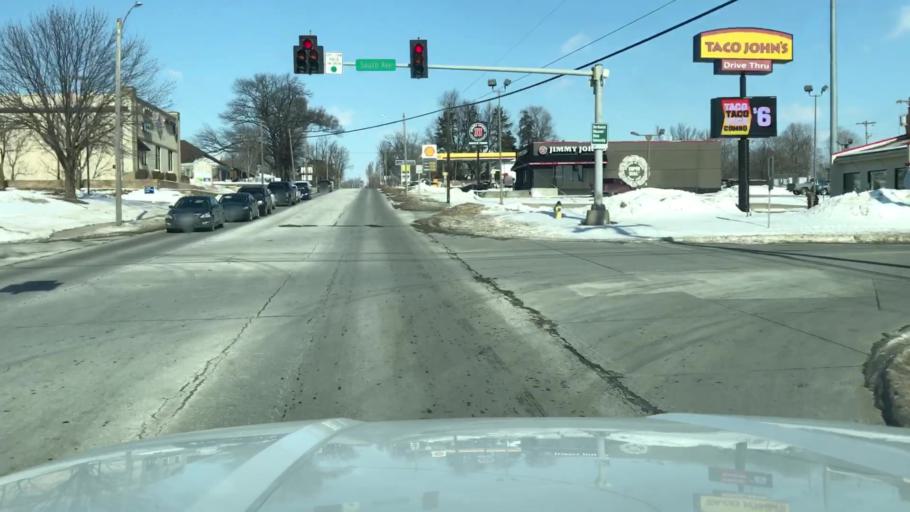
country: US
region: Missouri
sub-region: Nodaway County
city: Maryville
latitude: 40.3345
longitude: -94.8738
